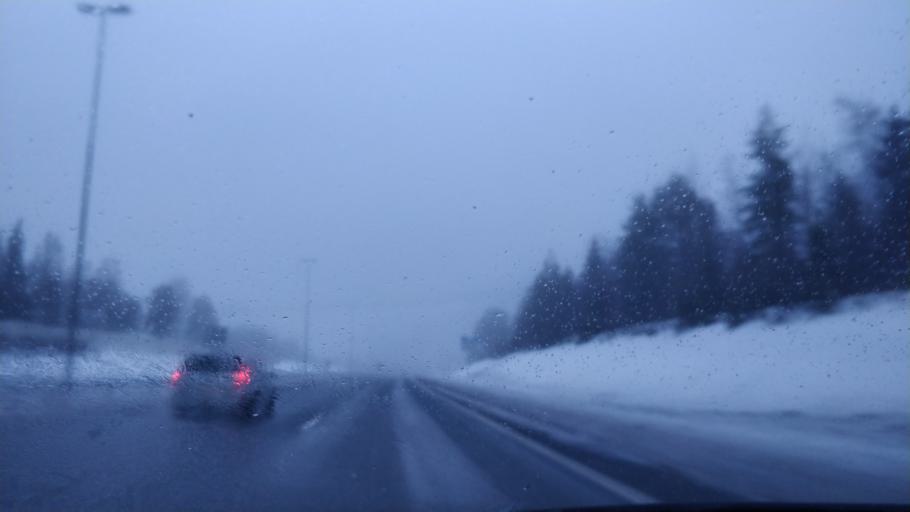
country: FI
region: Lapland
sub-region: Kemi-Tornio
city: Kemi
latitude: 65.7519
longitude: 24.5747
